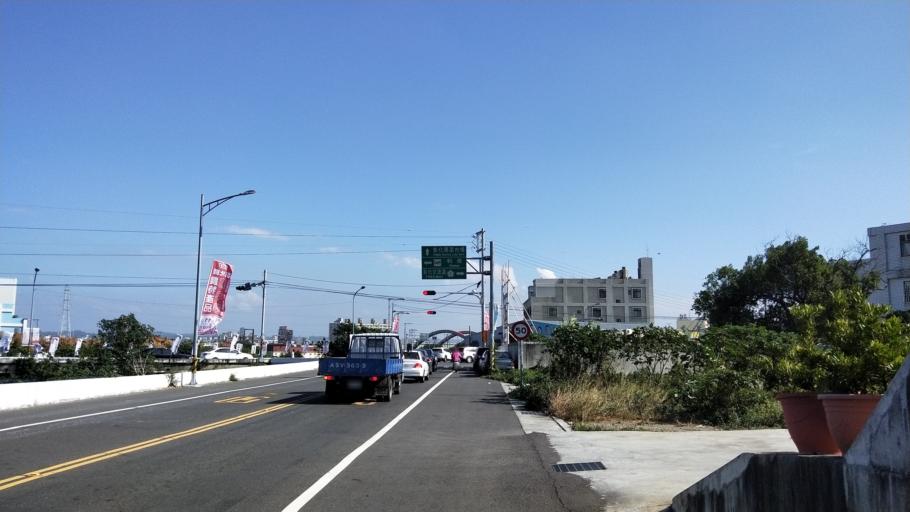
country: TW
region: Taiwan
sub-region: Changhua
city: Chang-hua
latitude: 24.0684
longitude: 120.5172
